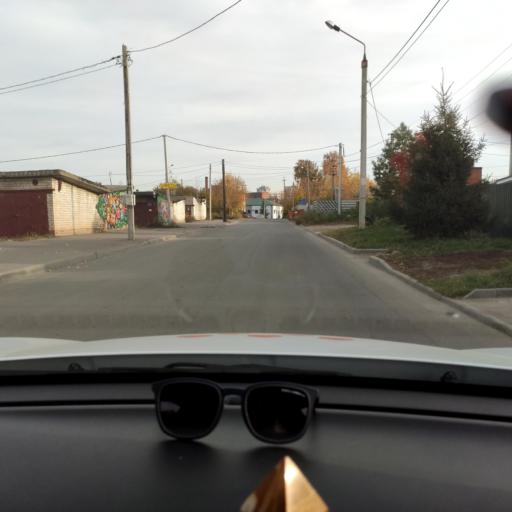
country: RU
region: Tatarstan
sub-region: Gorod Kazan'
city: Kazan
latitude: 55.8055
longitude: 49.0612
